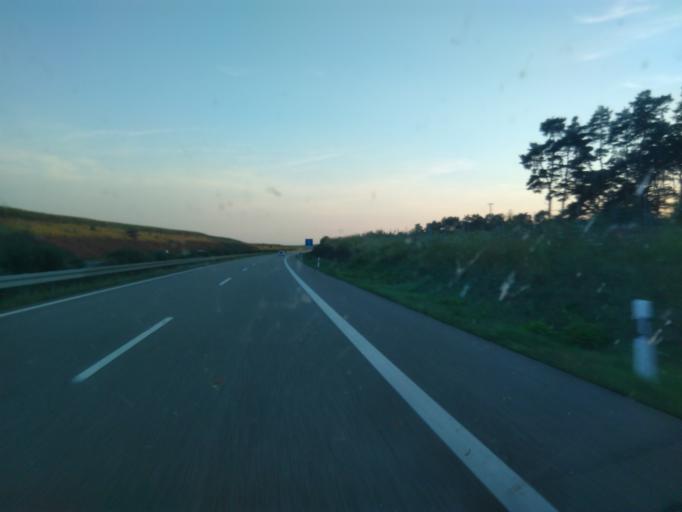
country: DE
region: Thuringia
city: Wolfershausen
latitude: 50.4377
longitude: 10.4348
